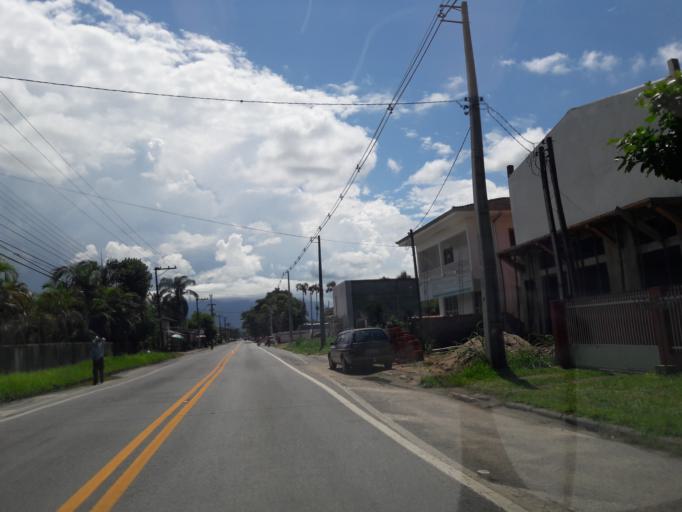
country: BR
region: Parana
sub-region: Antonina
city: Antonina
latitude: -25.4868
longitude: -48.8263
